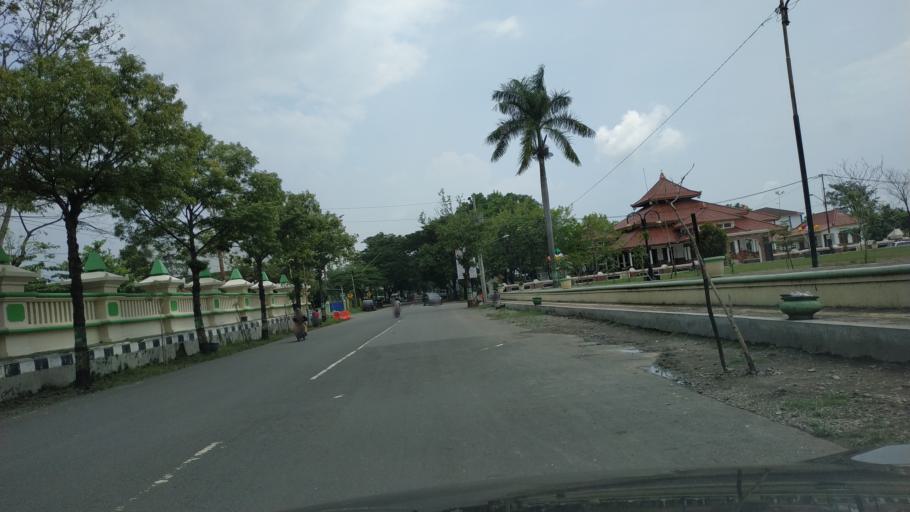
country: ID
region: Central Java
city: Slawi
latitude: -6.9938
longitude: 109.1273
